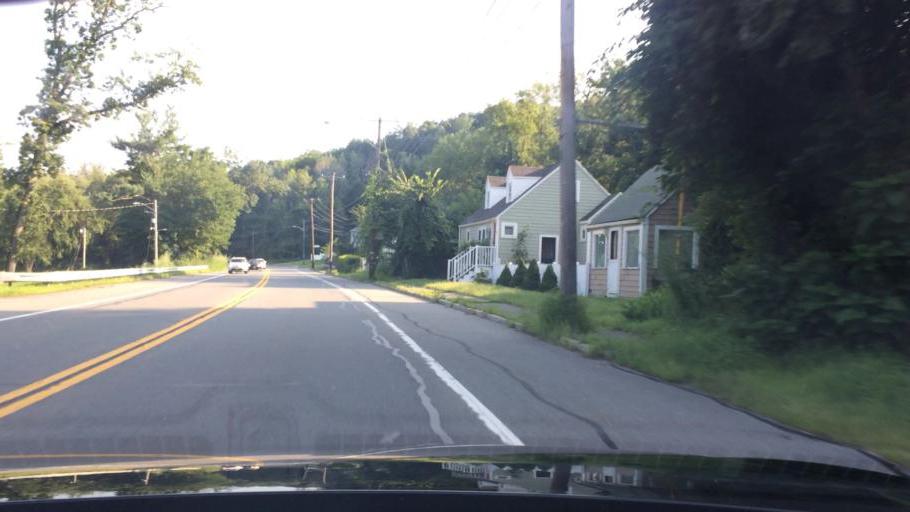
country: US
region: Massachusetts
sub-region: Essex County
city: Haverhill
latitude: 42.7713
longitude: -71.1328
